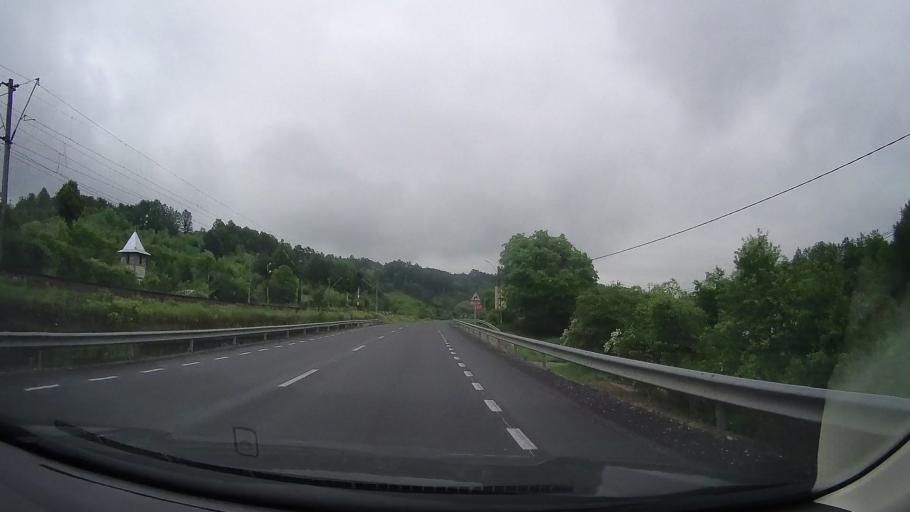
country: RO
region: Mehedinti
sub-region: Comuna Prunisor
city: Prunisor
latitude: 44.6147
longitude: 22.8549
